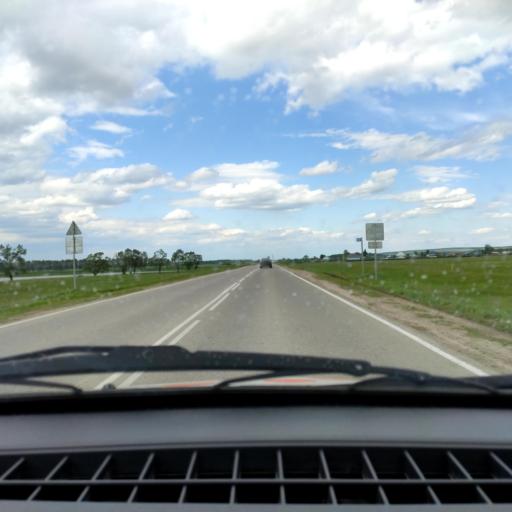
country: RU
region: Bashkortostan
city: Iglino
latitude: 54.9425
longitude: 56.4799
